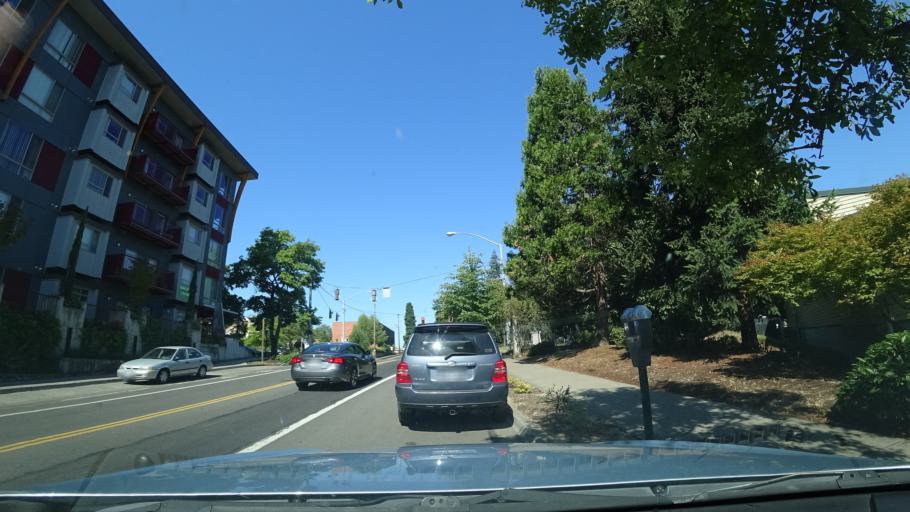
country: US
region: Oregon
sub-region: Lane County
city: Eugene
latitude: 44.0400
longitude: -123.0741
